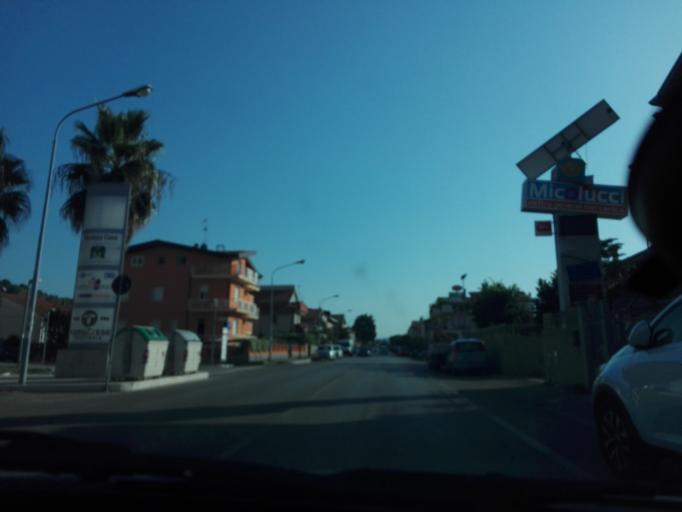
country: IT
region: Abruzzo
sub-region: Provincia di Pescara
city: Montesilvano Marina
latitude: 42.4984
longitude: 14.1302
